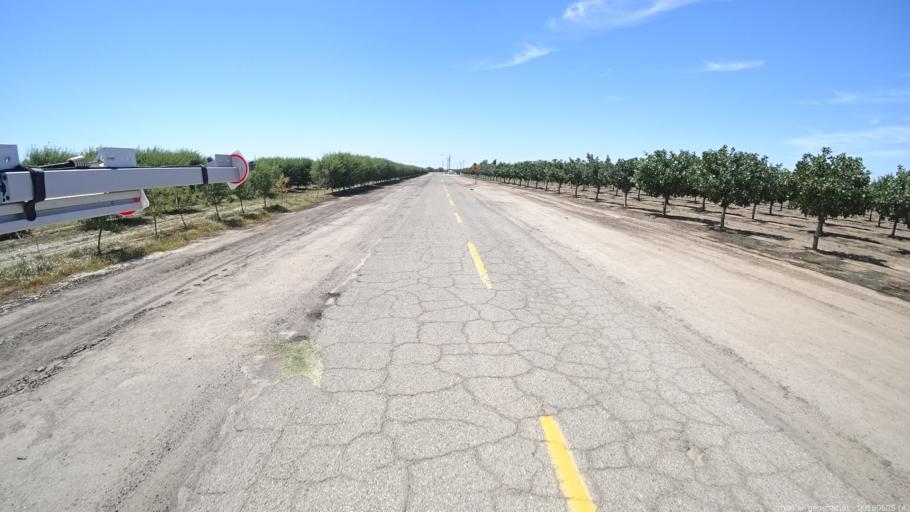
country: US
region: California
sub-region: Madera County
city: Chowchilla
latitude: 37.0867
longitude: -120.4554
